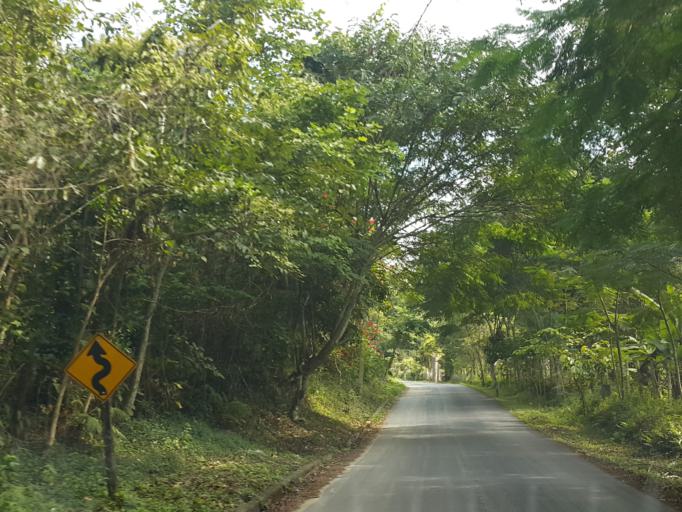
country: TH
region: Chiang Mai
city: Mae On
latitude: 18.8676
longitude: 99.3311
